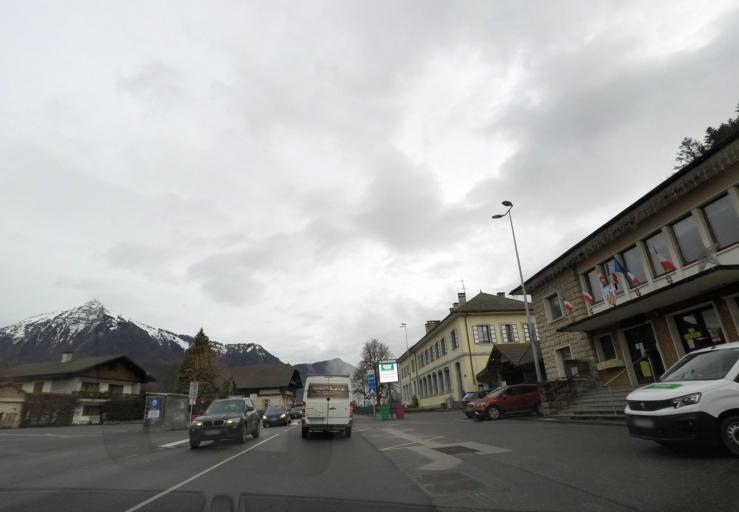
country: FR
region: Rhone-Alpes
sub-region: Departement de la Haute-Savoie
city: Chatillon-sur-Cluses
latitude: 46.0873
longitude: 6.5828
